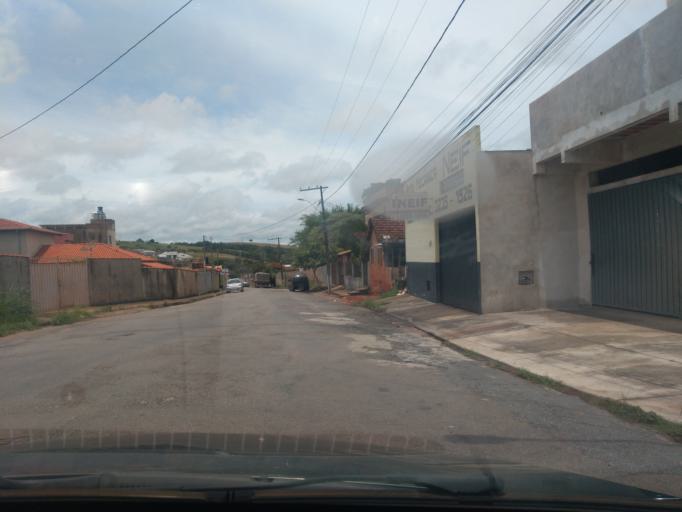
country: BR
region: Minas Gerais
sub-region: Tres Coracoes
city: Tres Coracoes
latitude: -21.6831
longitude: -45.2605
